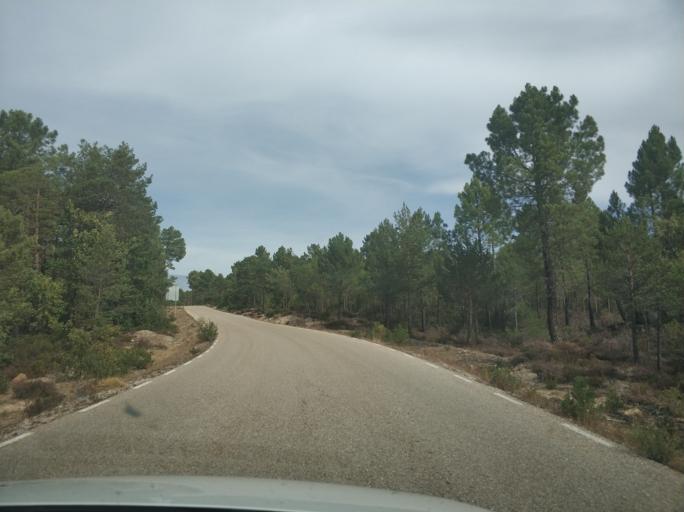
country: ES
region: Castille and Leon
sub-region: Provincia de Soria
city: Duruelo de la Sierra
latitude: 41.8812
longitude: -2.9362
